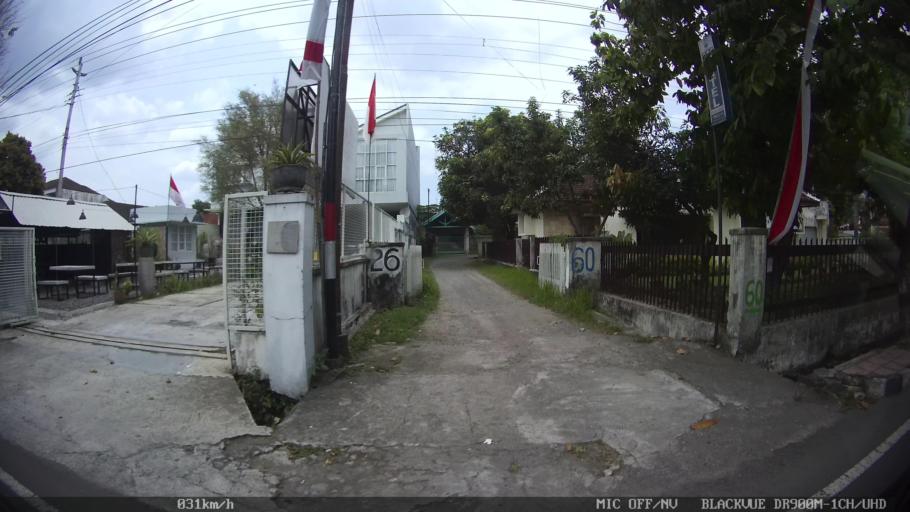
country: ID
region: Daerah Istimewa Yogyakarta
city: Yogyakarta
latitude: -7.7948
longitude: 110.3930
